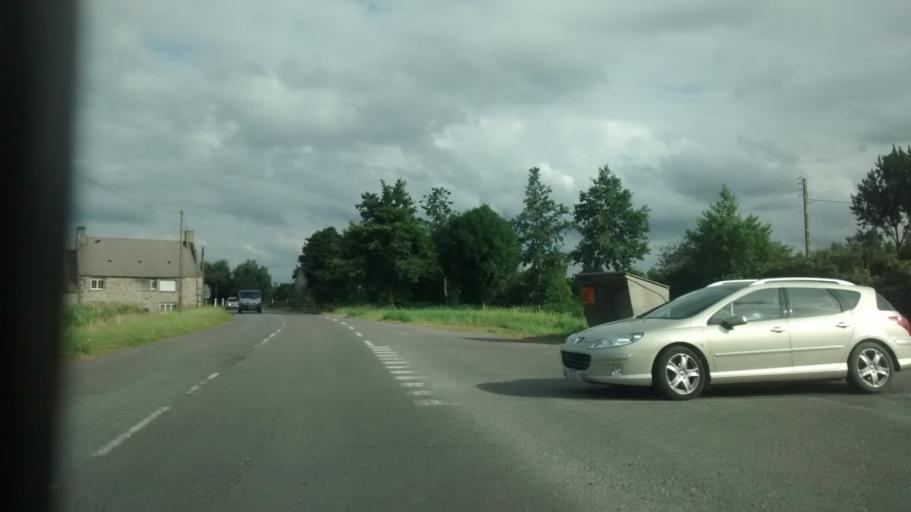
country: FR
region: Brittany
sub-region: Departement d'Ille-et-Vilaine
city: Dol-de-Bretagne
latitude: 48.5656
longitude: -1.7713
